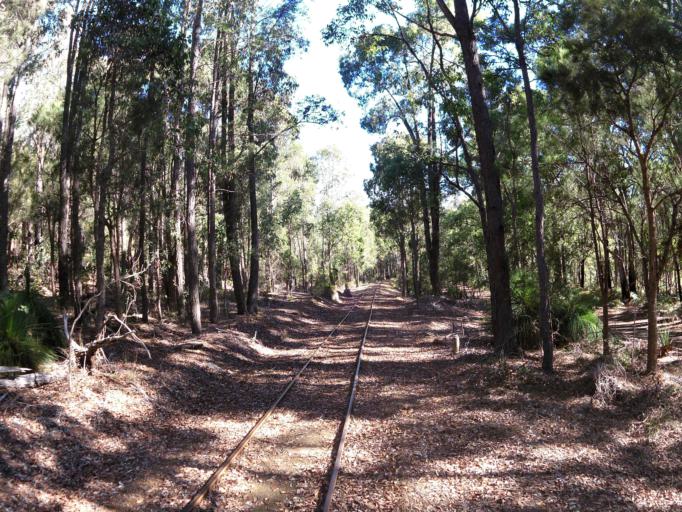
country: AU
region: Western Australia
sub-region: Waroona
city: Waroona
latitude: -32.7108
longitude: 116.0776
